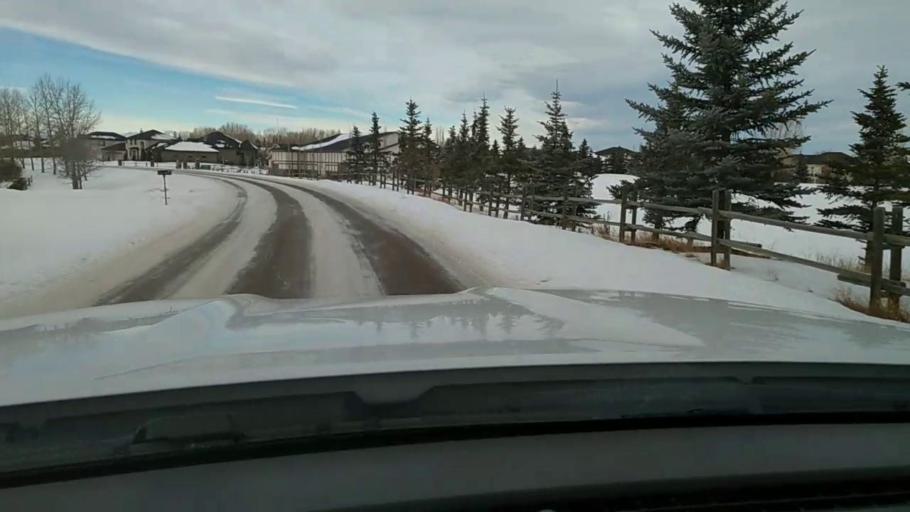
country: CA
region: Alberta
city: Calgary
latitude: 51.1168
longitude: -114.2598
